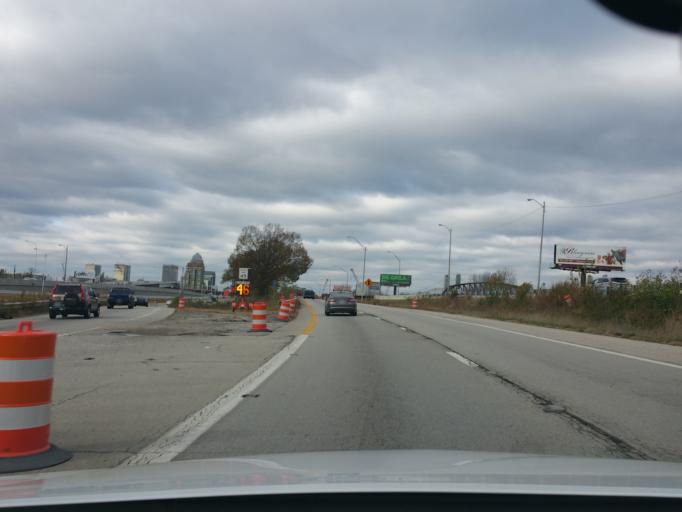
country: US
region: Indiana
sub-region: Clark County
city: Jeffersonville
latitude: 38.2623
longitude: -85.7296
